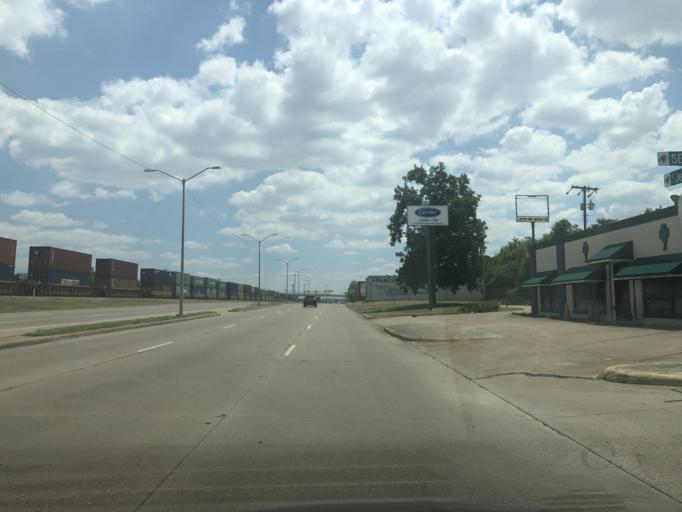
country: US
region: Texas
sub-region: Dallas County
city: Grand Prairie
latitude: 32.7446
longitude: -97.0014
